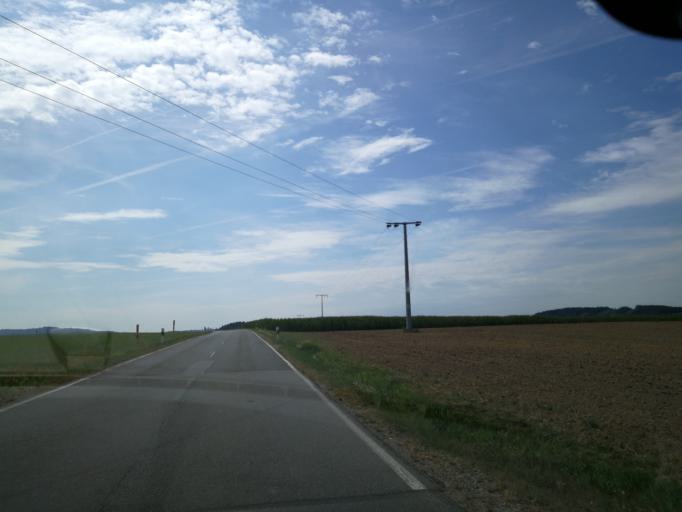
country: DE
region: Bavaria
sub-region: Upper Palatinate
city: Falkenstein
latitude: 49.0750
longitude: 12.5113
